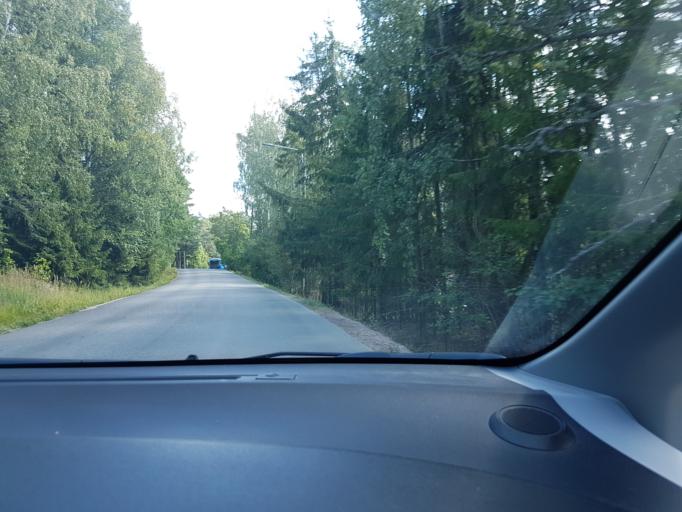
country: FI
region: Uusimaa
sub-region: Helsinki
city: Kilo
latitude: 60.3392
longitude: 24.8080
